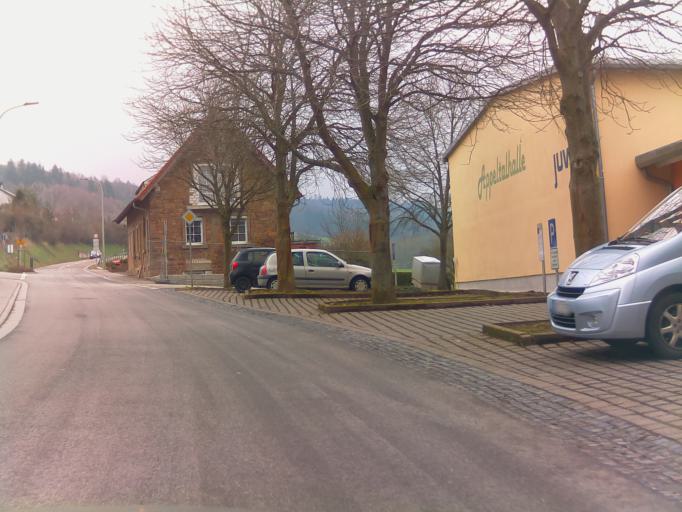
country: DE
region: Rheinland-Pfalz
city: Gerbach
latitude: 49.6726
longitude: 7.8737
